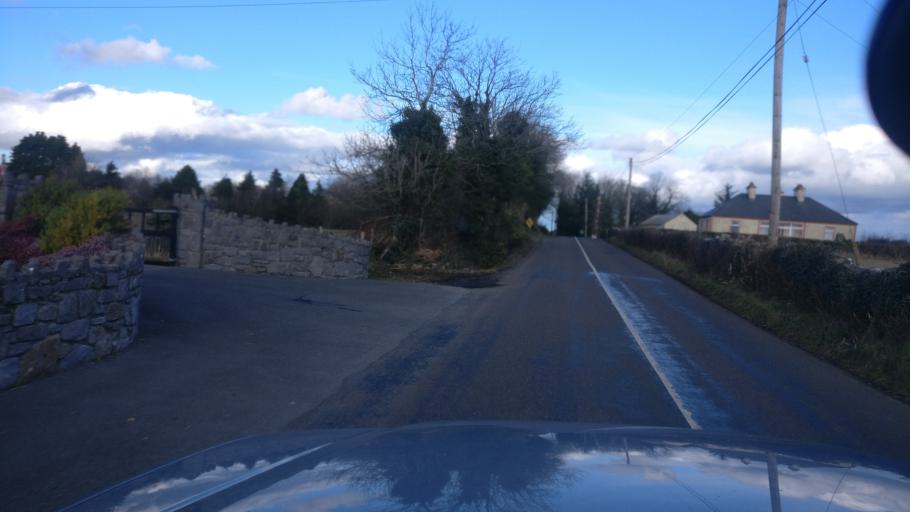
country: IE
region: Connaught
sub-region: County Galway
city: Loughrea
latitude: 53.2150
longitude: -8.3985
